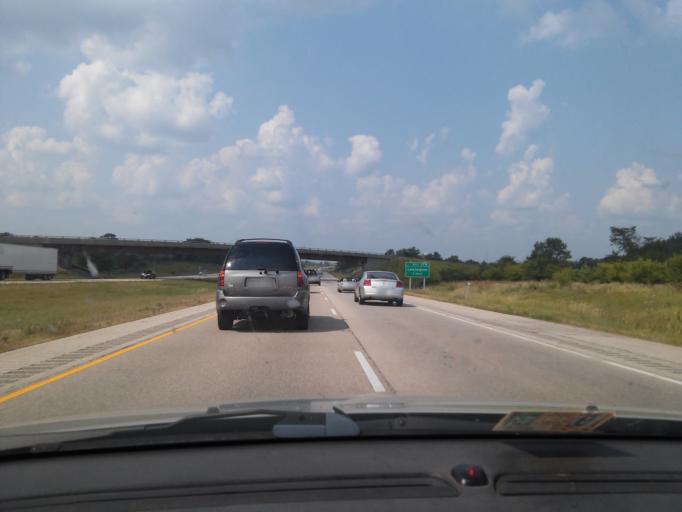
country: US
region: Illinois
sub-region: McLean County
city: Lexington
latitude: 40.6242
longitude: -88.8178
